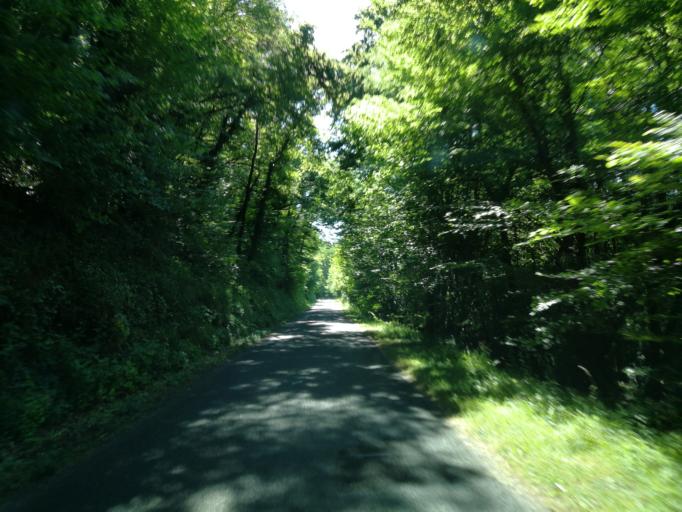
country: FR
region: Aquitaine
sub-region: Departement de la Dordogne
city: Eyvigues-et-Eybenes
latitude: 44.8759
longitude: 1.3922
